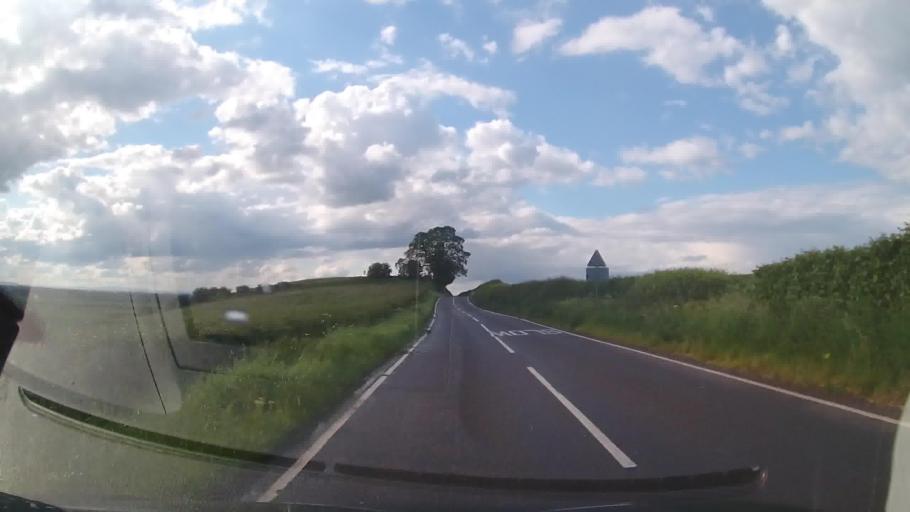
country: GB
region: England
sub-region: Shropshire
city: Withington
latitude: 52.6589
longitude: -2.6181
